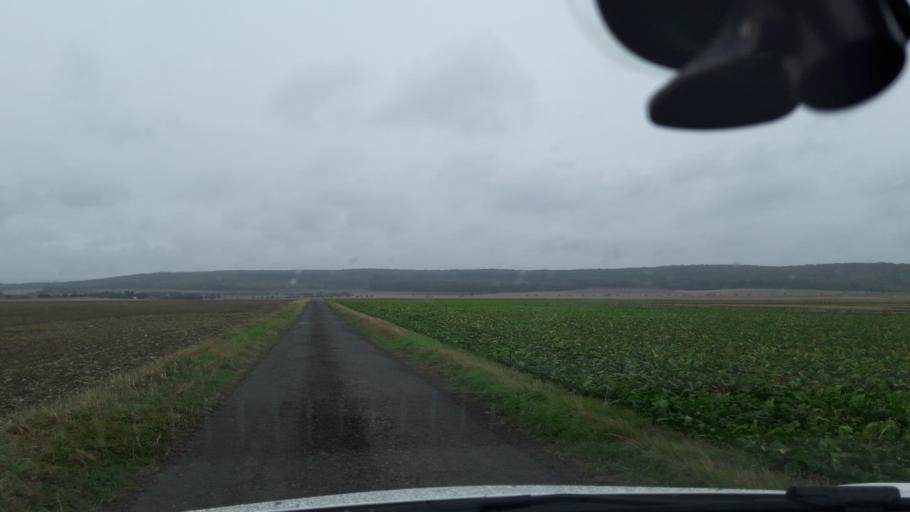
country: DE
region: Lower Saxony
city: Schladen
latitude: 51.9980
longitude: 10.5374
